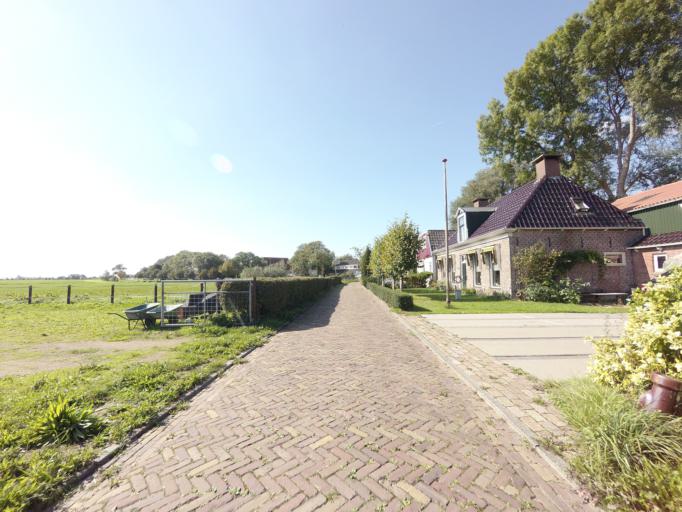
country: NL
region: Friesland
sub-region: Gemeente Littenseradiel
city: Makkum
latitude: 53.1123
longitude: 5.6736
